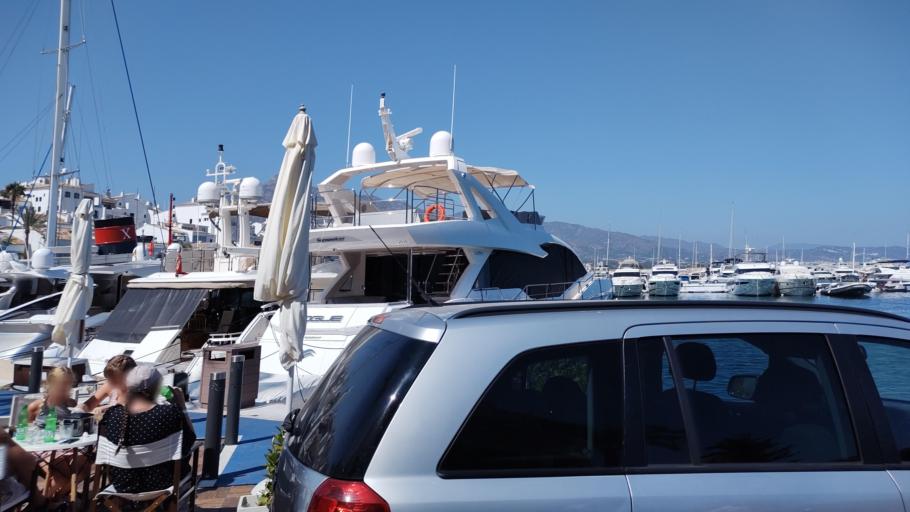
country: ES
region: Andalusia
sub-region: Provincia de Malaga
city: Marbella
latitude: 36.4853
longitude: -4.9541
